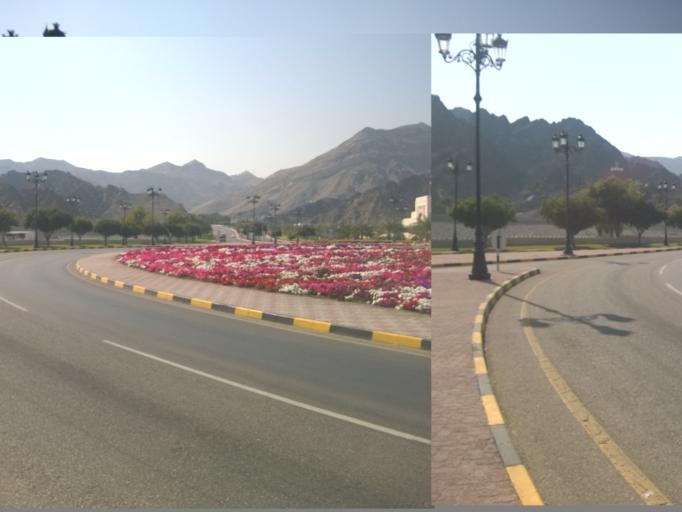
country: OM
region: Muhafazat Masqat
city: Muscat
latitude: 23.5674
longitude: 58.6086
